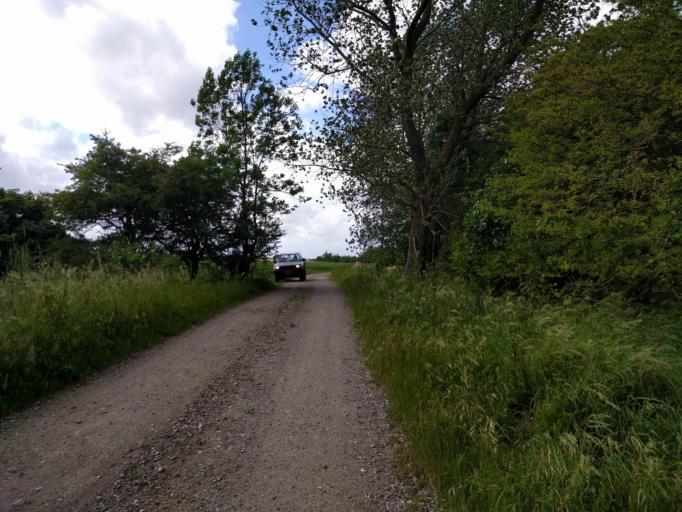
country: DK
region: South Denmark
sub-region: Kerteminde Kommune
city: Munkebo
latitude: 55.4652
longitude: 10.5139
